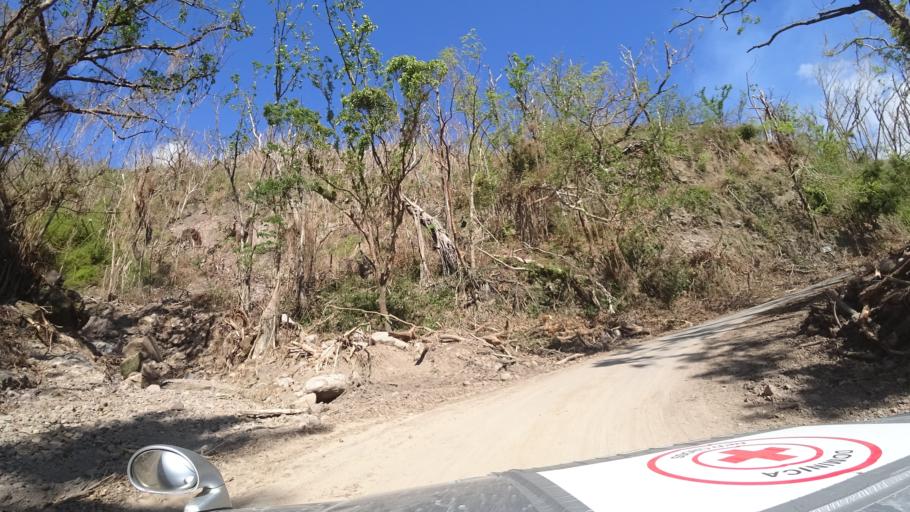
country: DM
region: Saint Mark
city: Soufriere
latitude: 15.2380
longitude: -61.3644
